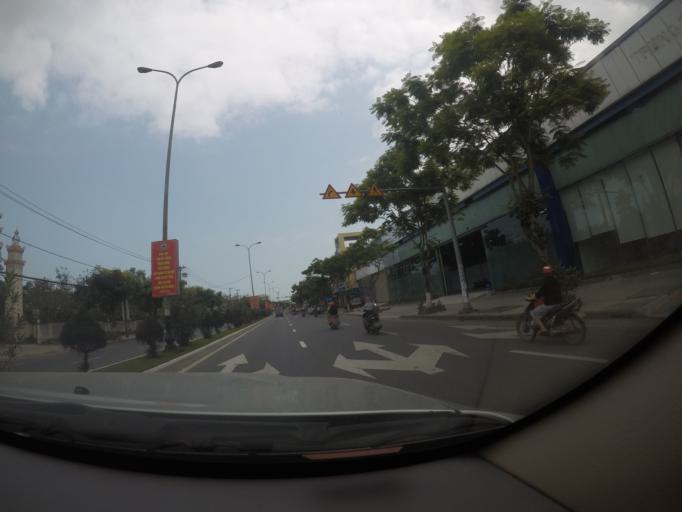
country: VN
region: Da Nang
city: Lien Chieu
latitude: 16.0597
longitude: 108.1636
